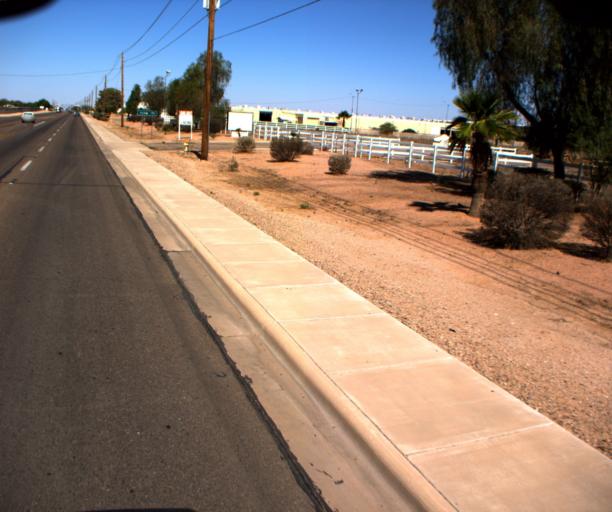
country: US
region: Arizona
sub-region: Pinal County
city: Casa Grande
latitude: 32.8795
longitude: -111.7771
